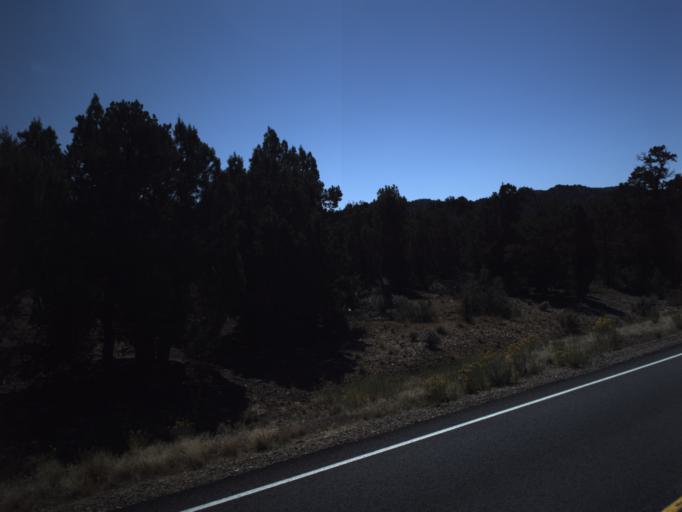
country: US
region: Utah
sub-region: Garfield County
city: Panguitch
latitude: 37.6199
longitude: -111.8736
